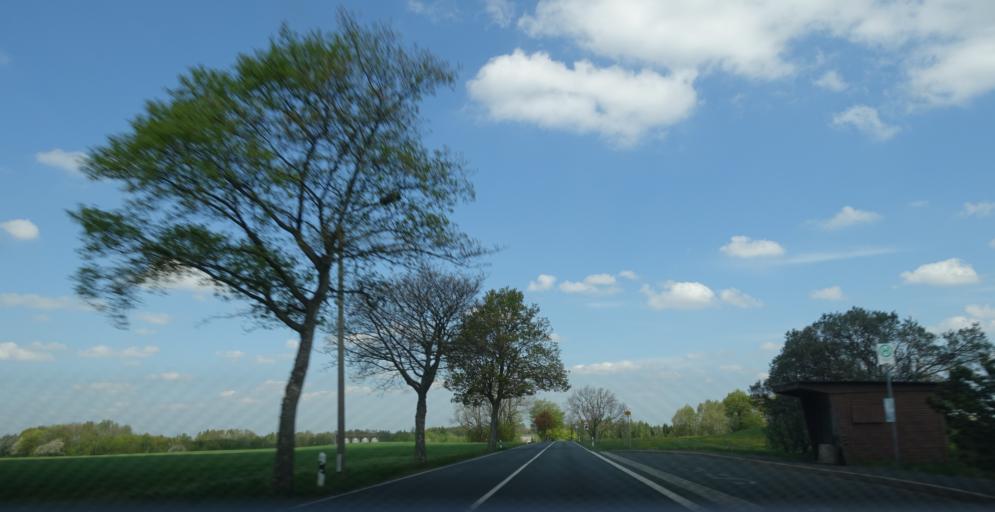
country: DE
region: Saxony
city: Brand-Erbisdorf
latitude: 50.8443
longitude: 13.3217
